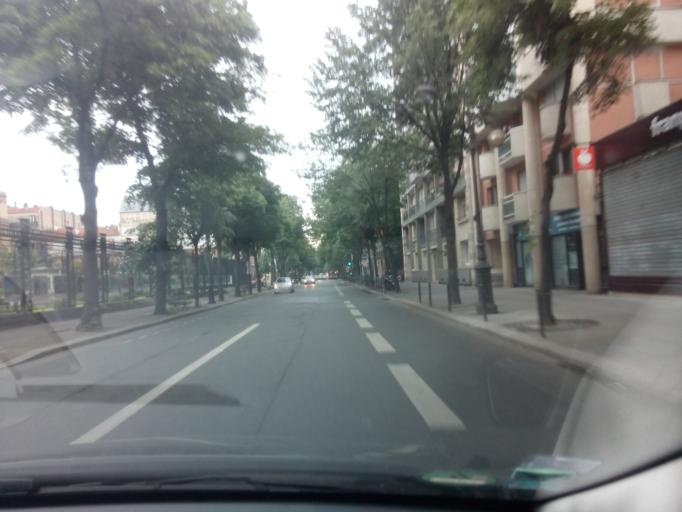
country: FR
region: Ile-de-France
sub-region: Departement des Hauts-de-Seine
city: Vanves
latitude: 48.8447
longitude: 2.2802
